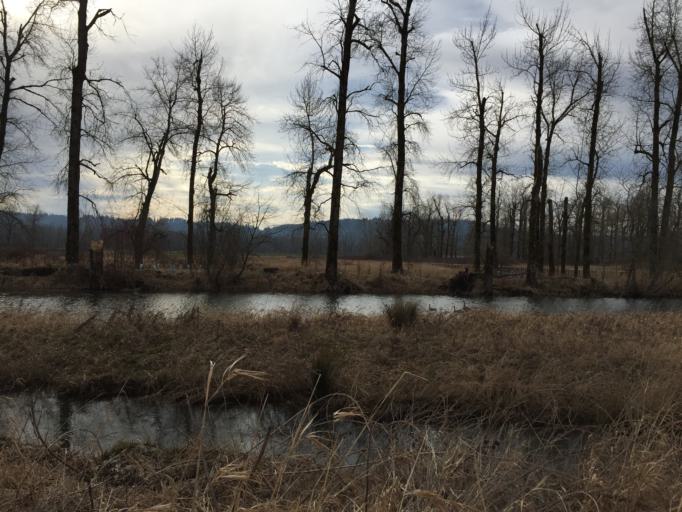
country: US
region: Washington
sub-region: Clark County
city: Washougal
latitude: 45.5635
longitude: -122.3138
